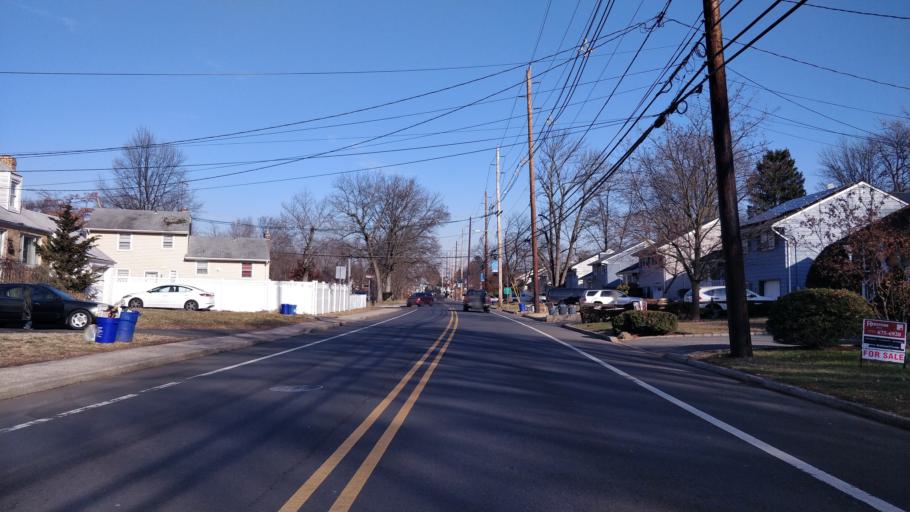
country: US
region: New Jersey
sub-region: Somerset County
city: North Plainfield
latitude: 40.6208
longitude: -74.4388
